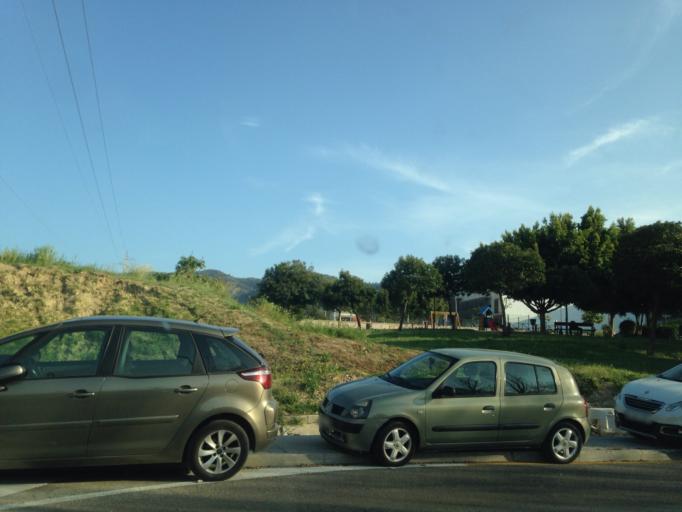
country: ES
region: Andalusia
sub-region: Provincia de Malaga
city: Alhaurin de la Torre
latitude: 36.6625
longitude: -4.5581
